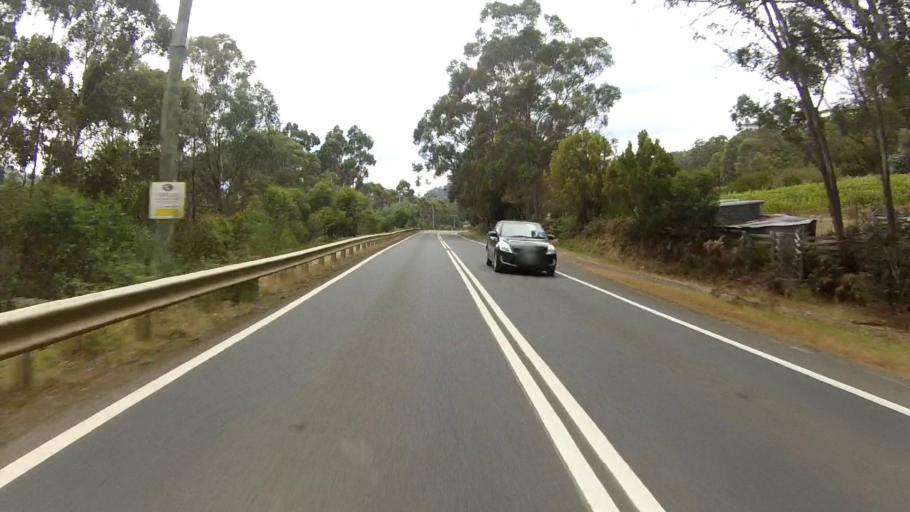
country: AU
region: Tasmania
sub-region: Huon Valley
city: Huonville
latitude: -43.0596
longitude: 147.0430
